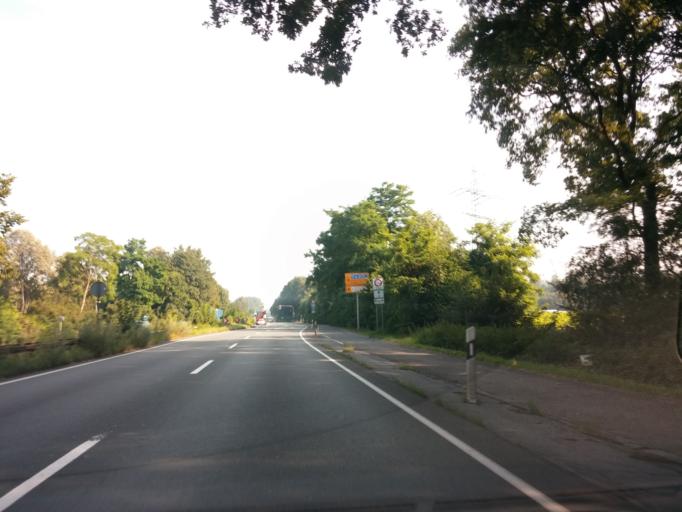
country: DE
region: North Rhine-Westphalia
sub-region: Regierungsbezirk Munster
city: Gladbeck
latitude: 51.5415
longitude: 6.9840
